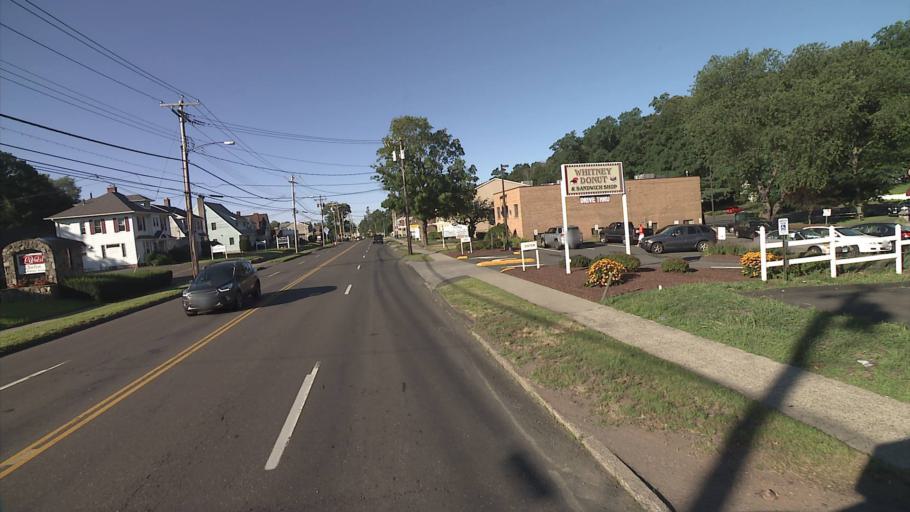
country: US
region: Connecticut
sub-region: New Haven County
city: Hamden
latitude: 41.3904
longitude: -72.8988
